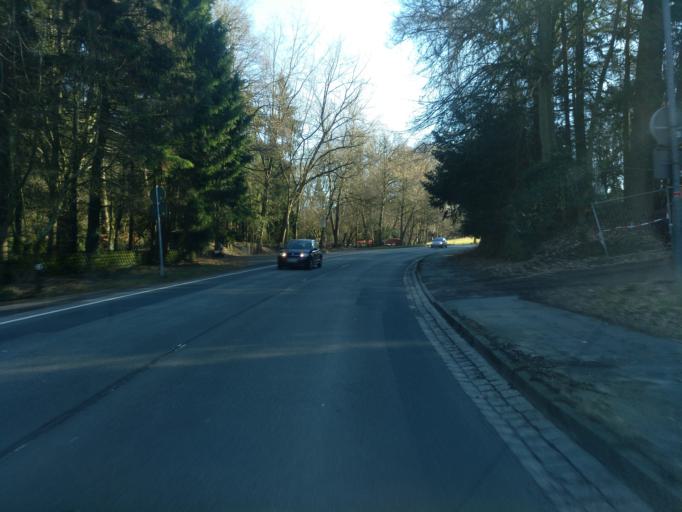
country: DE
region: Hamburg
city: Harburg
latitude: 53.4523
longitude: 9.9050
